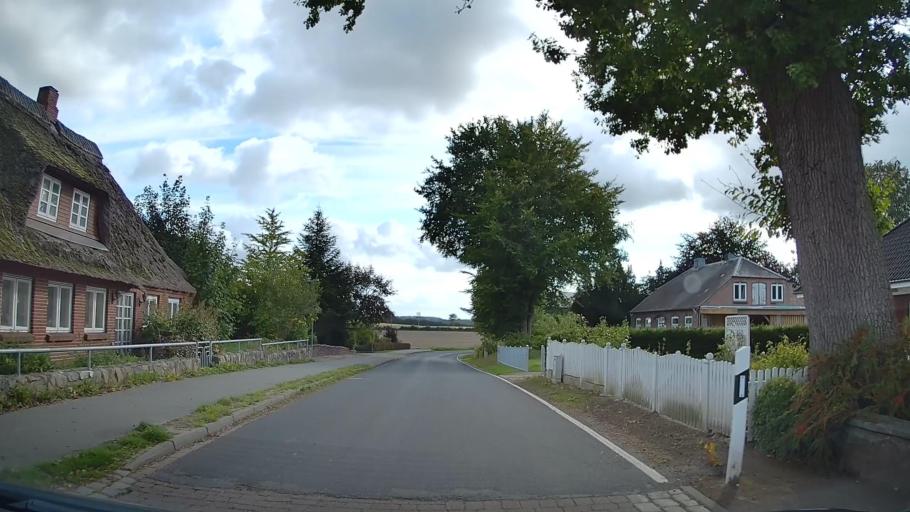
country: DE
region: Schleswig-Holstein
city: Niesgrau
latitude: 54.7675
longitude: 9.8068
